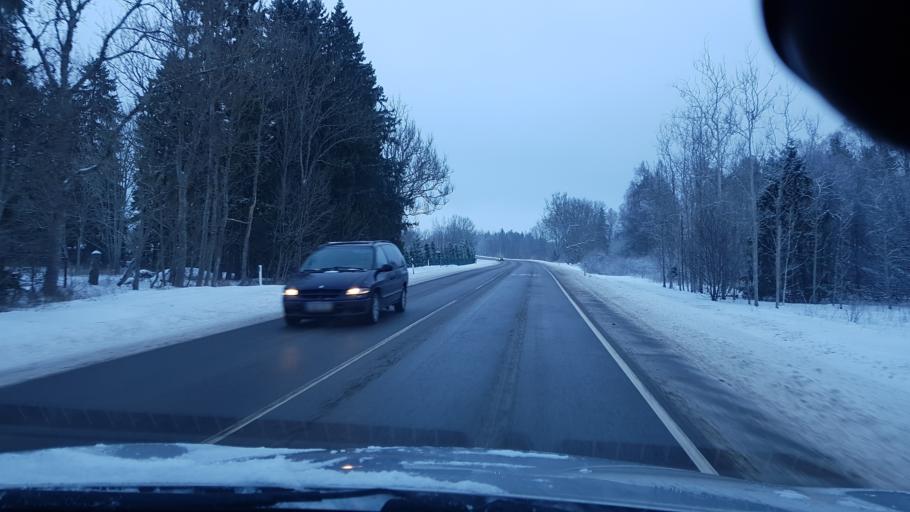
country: EE
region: Harju
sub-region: Keila linn
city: Keila
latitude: 59.3396
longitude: 24.2709
